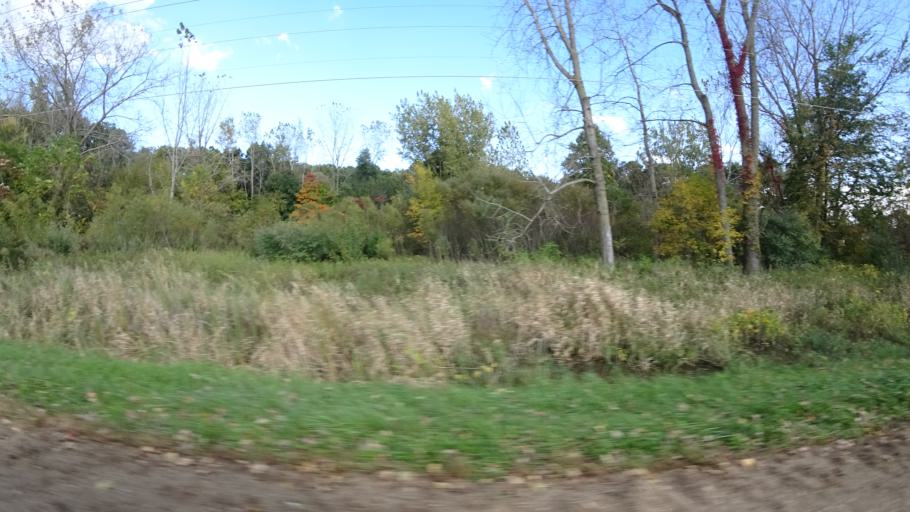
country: US
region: Michigan
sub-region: Saint Joseph County
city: Centreville
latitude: 41.9467
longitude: -85.5277
